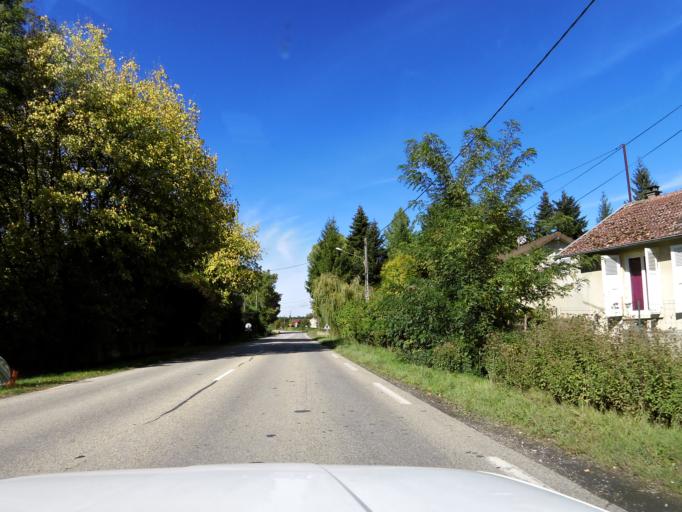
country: FR
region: Rhone-Alpes
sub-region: Departement de l'Isere
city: Bouvesse-Quirieu
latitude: 45.8047
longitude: 5.4137
